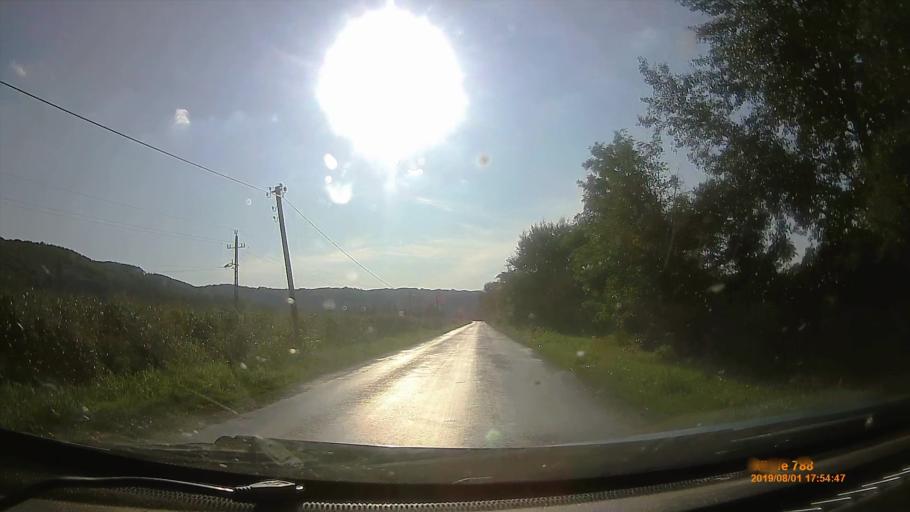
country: HU
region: Baranya
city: Sasd
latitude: 46.1928
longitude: 18.1460
